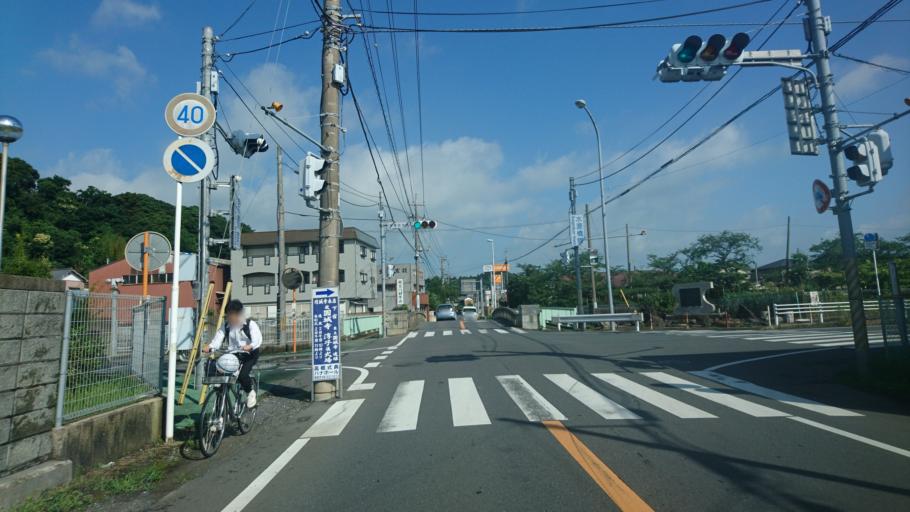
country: JP
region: Chiba
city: Katori-shi
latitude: 35.8962
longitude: 140.4888
